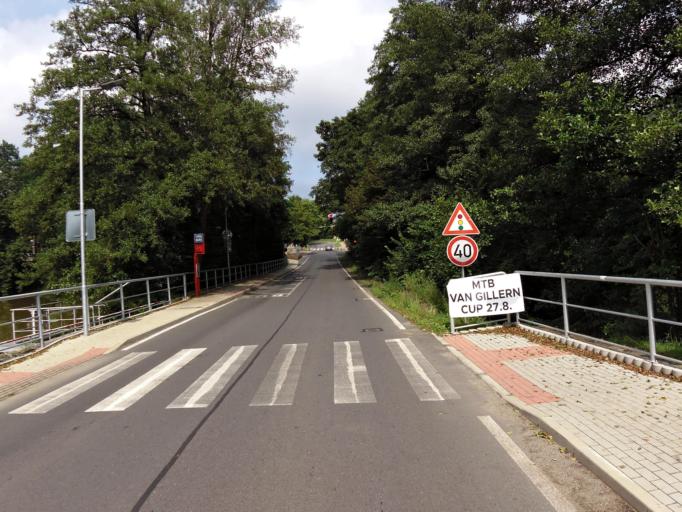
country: CZ
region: Central Bohemia
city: Kamenice
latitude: 49.9002
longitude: 14.5814
